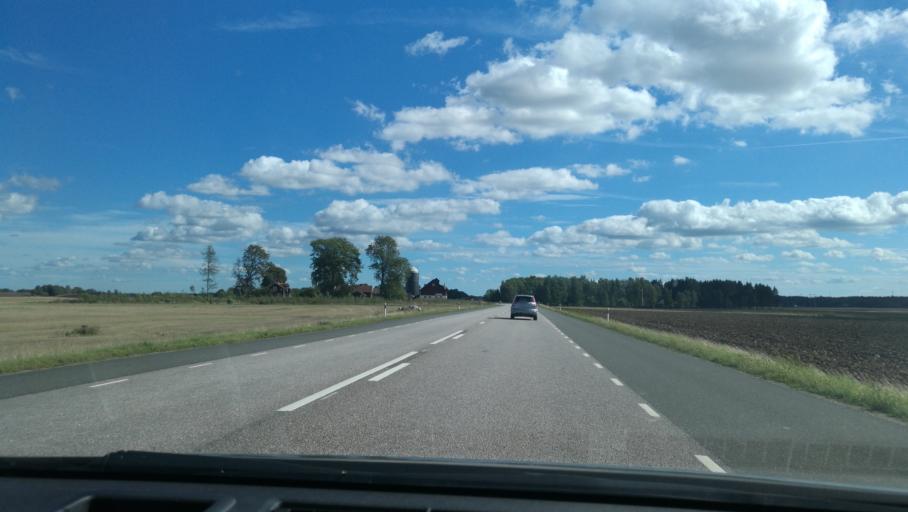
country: SE
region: Vaestra Goetaland
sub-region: Gotene Kommun
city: Kallby
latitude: 58.5092
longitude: 13.3796
